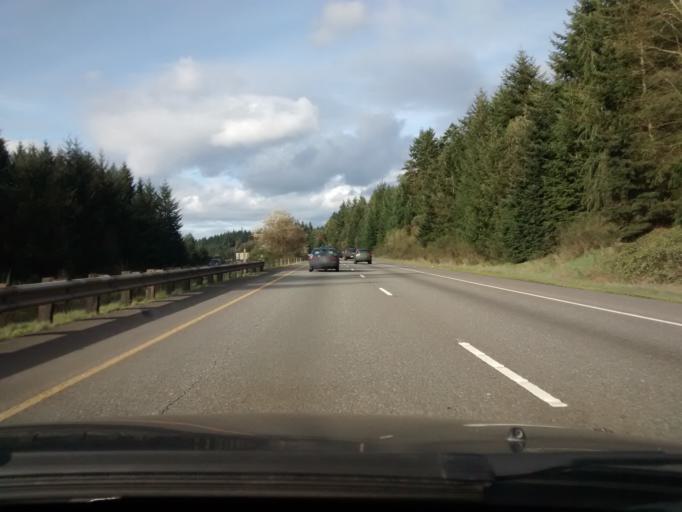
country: US
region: Washington
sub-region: Pierce County
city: Purdy
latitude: 47.3746
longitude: -122.6173
